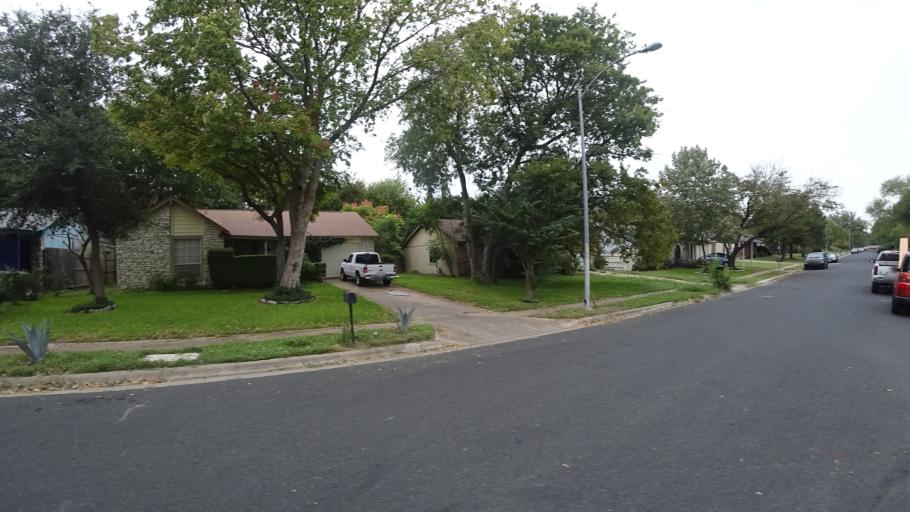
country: US
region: Texas
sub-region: Travis County
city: Onion Creek
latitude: 30.1997
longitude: -97.7790
